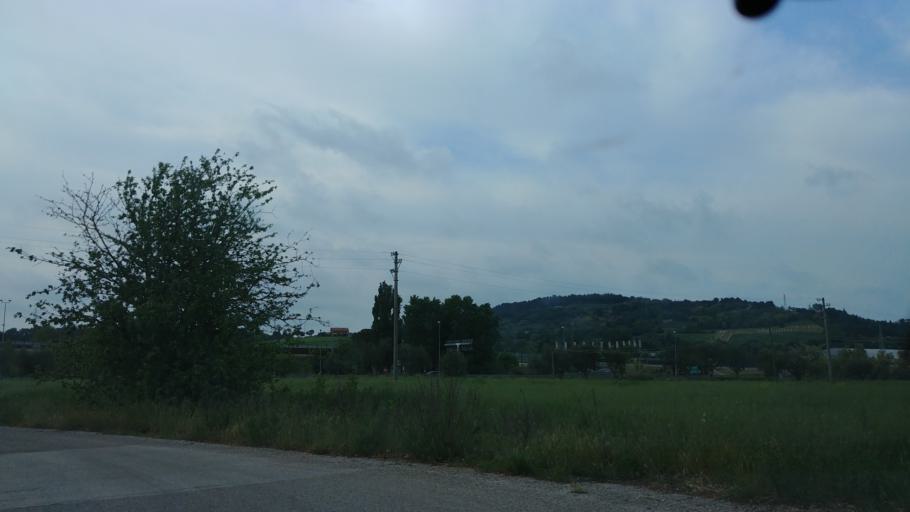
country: IT
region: The Marches
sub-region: Provincia di Pesaro e Urbino
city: Villa Ceccolini
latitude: 43.8967
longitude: 12.8431
